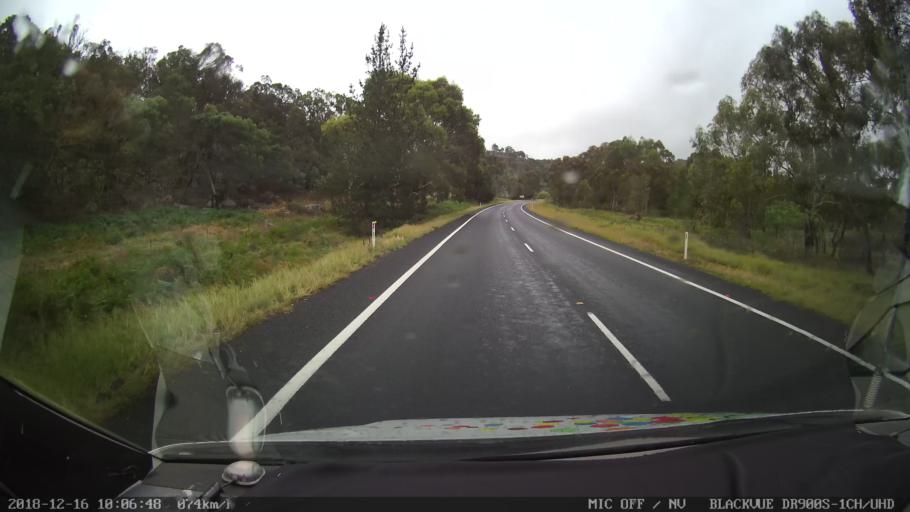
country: AU
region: New South Wales
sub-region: Glen Innes Severn
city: Glen Innes
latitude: -29.3414
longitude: 151.8924
